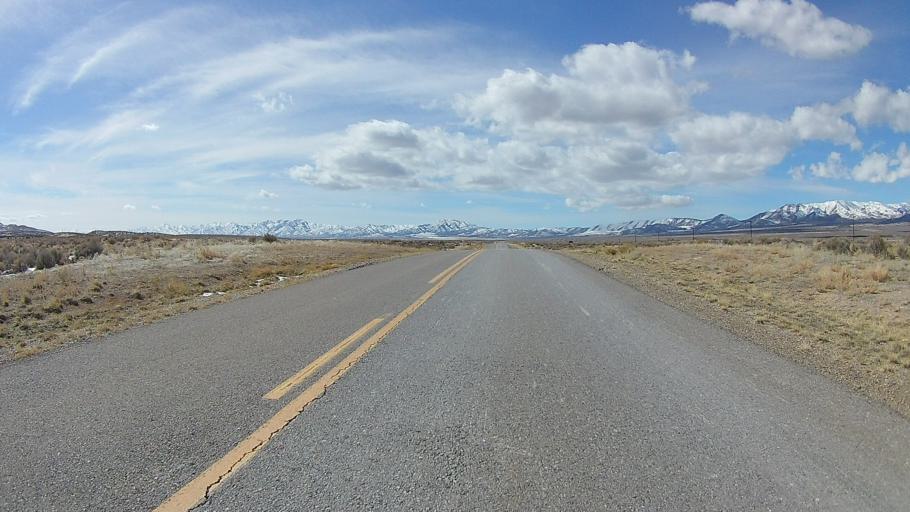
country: US
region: Utah
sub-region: Tooele County
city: Tooele
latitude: 40.1809
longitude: -112.3958
